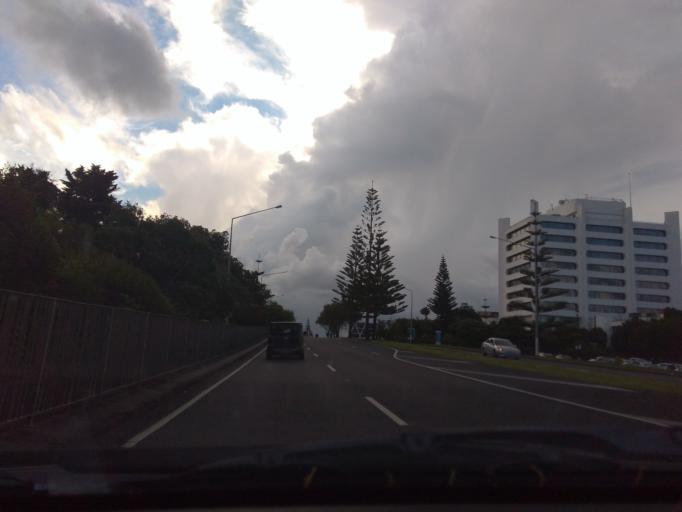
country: NZ
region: Auckland
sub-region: Auckland
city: Manukau City
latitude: -36.9933
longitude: 174.8823
